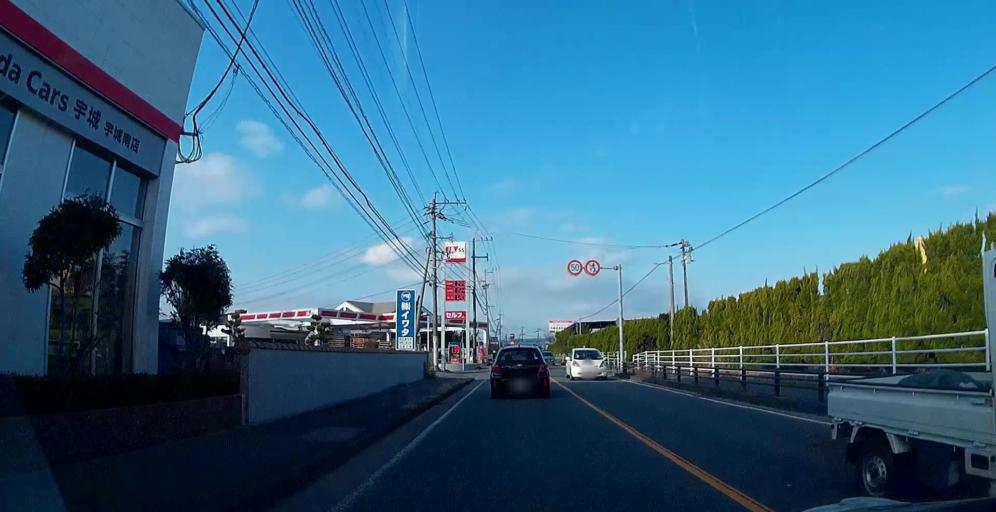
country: JP
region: Kumamoto
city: Matsubase
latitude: 32.6019
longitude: 130.7022
